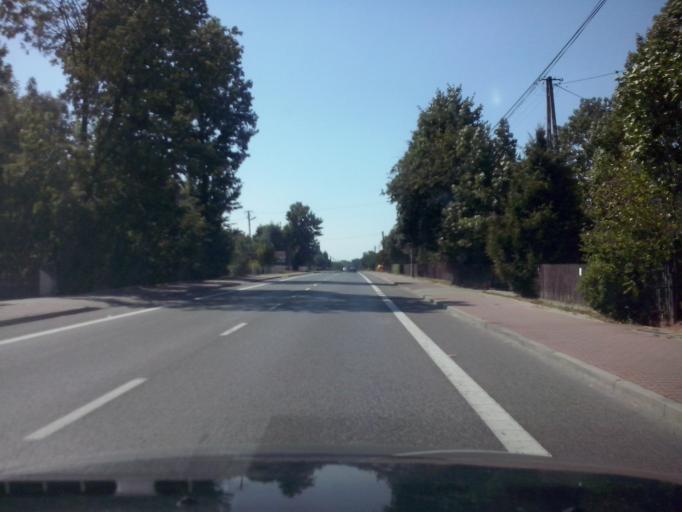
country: PL
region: Swietokrzyskie
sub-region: Powiat kielecki
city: Bieliny
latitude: 50.8492
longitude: 20.9163
